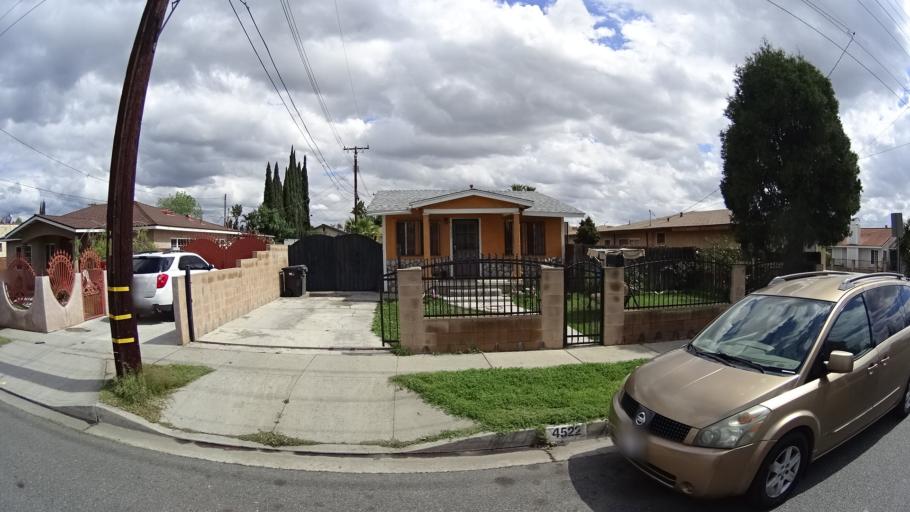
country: US
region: California
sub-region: Los Angeles County
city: Baldwin Park
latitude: 34.0945
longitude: -117.9780
